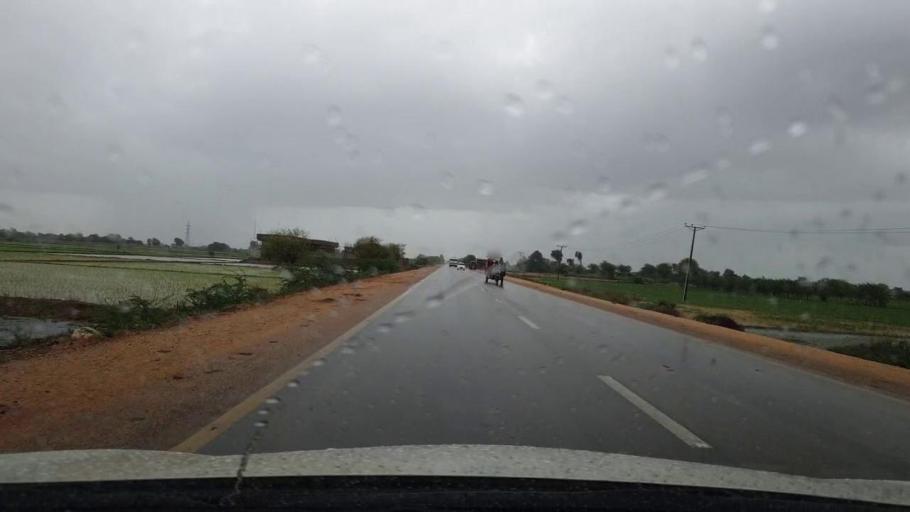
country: PK
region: Sindh
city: Kario
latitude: 24.6531
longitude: 68.5934
